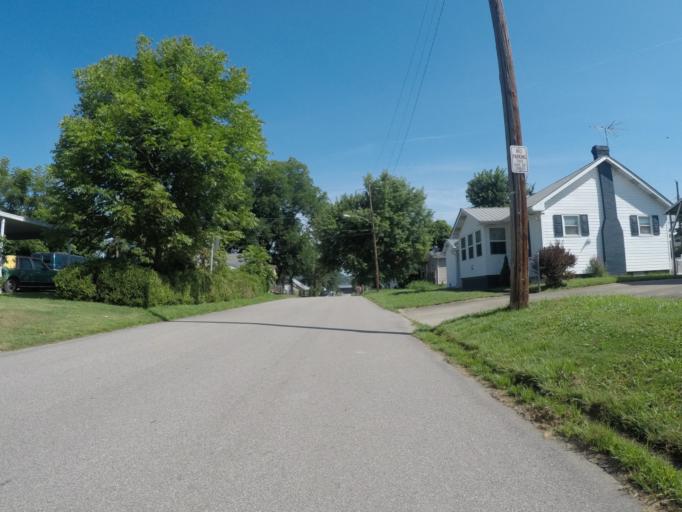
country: US
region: West Virginia
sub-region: Cabell County
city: Huntington
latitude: 38.4069
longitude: -82.4845
